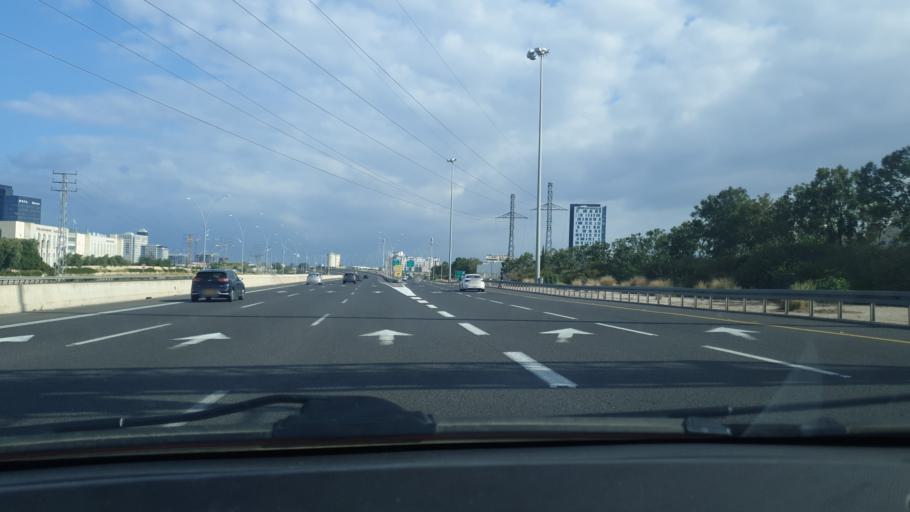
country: IL
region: Central District
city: Ra'anana
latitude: 32.1858
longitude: 34.8901
